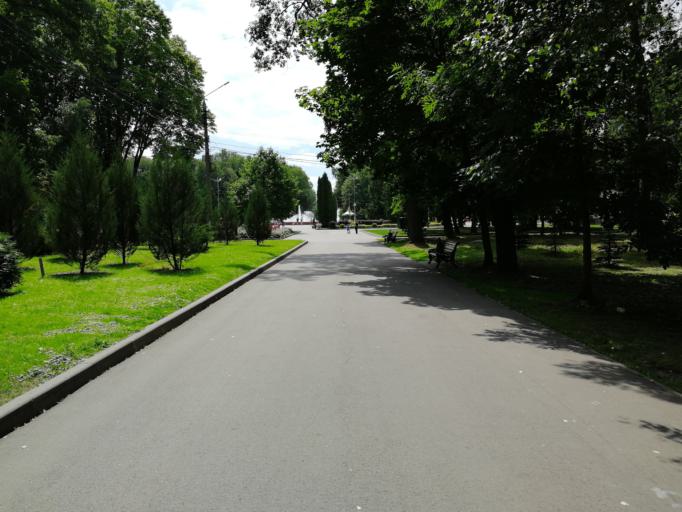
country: RU
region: Tula
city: Tula
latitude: 54.1844
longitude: 37.5931
